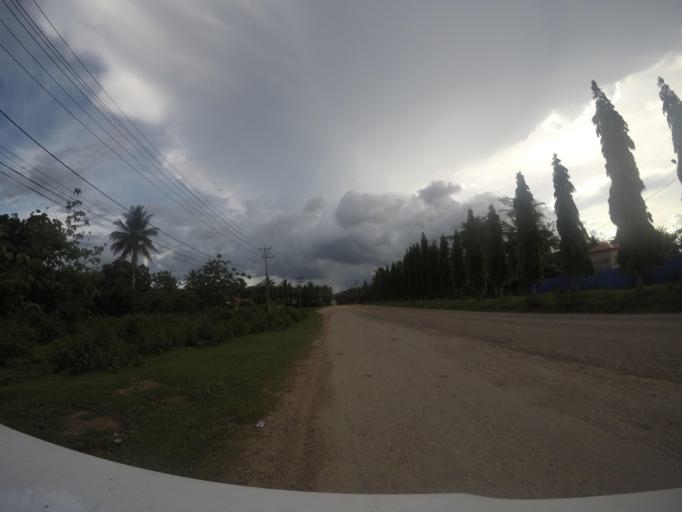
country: TL
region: Lautem
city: Lospalos
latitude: -8.4961
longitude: 126.9919
